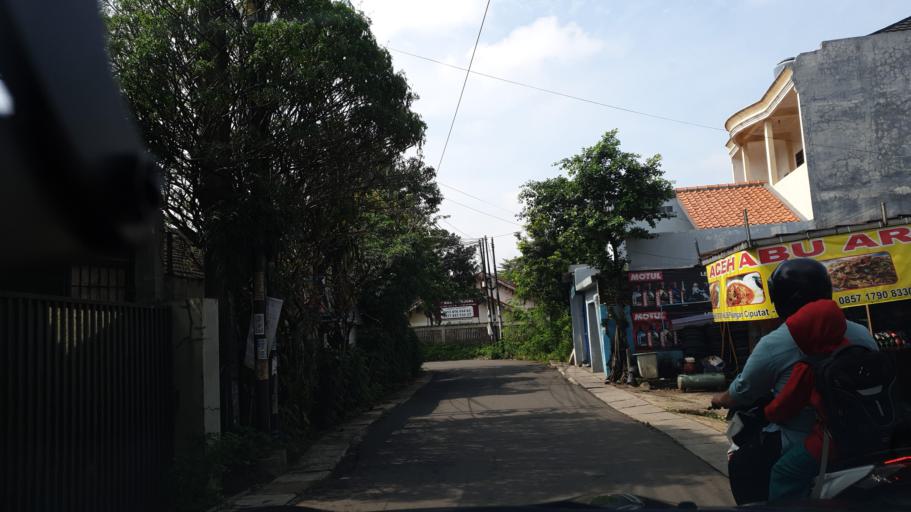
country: ID
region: West Java
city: Pamulang
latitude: -6.3216
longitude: 106.7554
